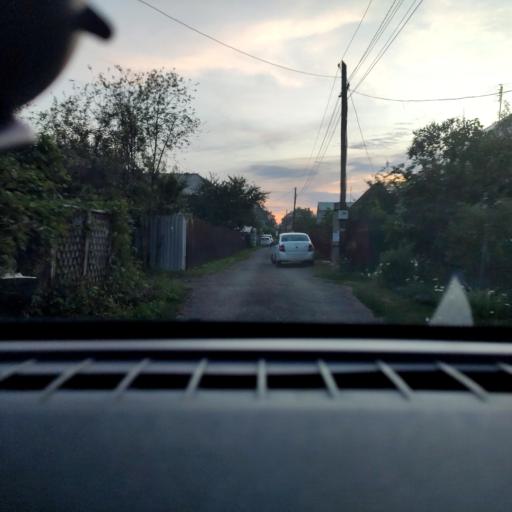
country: RU
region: Samara
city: Tol'yatti
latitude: 53.6320
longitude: 49.4084
